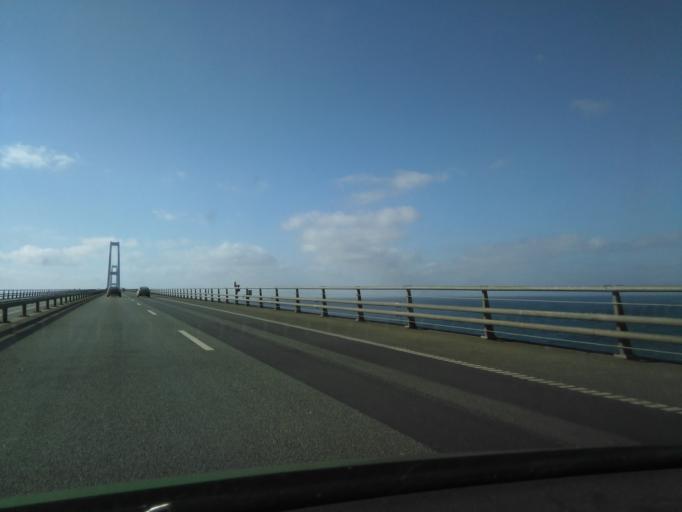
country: DK
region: Zealand
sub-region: Slagelse Kommune
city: Korsor
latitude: 55.3482
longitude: 11.0847
